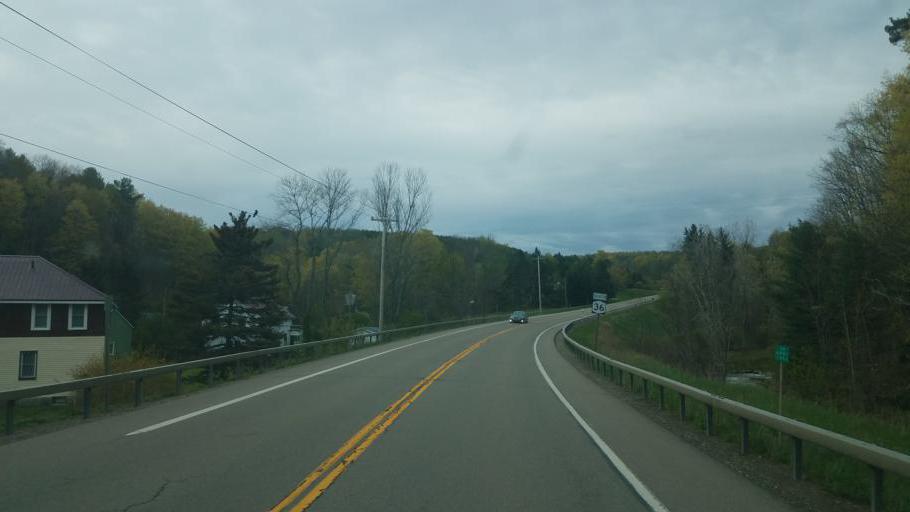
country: US
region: New York
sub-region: Steuben County
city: Canisteo
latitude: 42.1958
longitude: -77.5512
